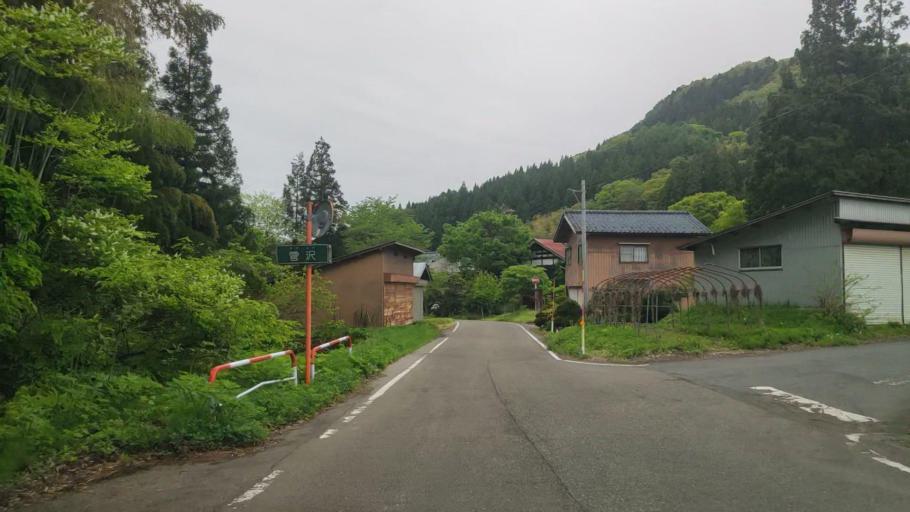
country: JP
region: Niigata
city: Gosen
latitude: 37.7125
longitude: 139.1045
